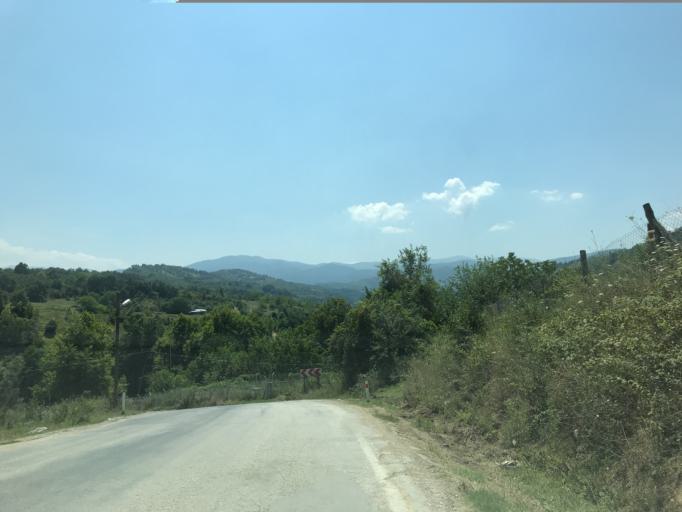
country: TR
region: Bursa
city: Tahtakopru
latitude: 39.9844
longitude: 29.6068
